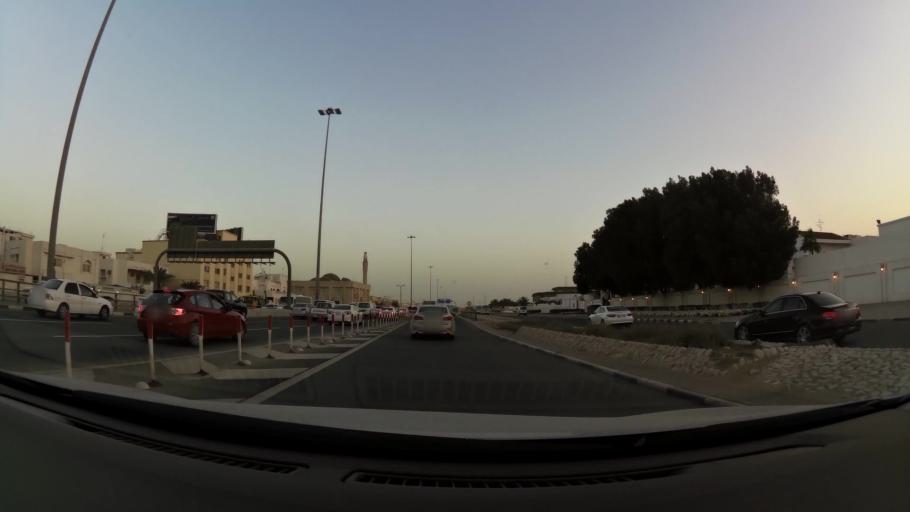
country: QA
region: Baladiyat ar Rayyan
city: Ar Rayyan
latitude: 25.3163
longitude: 51.4707
